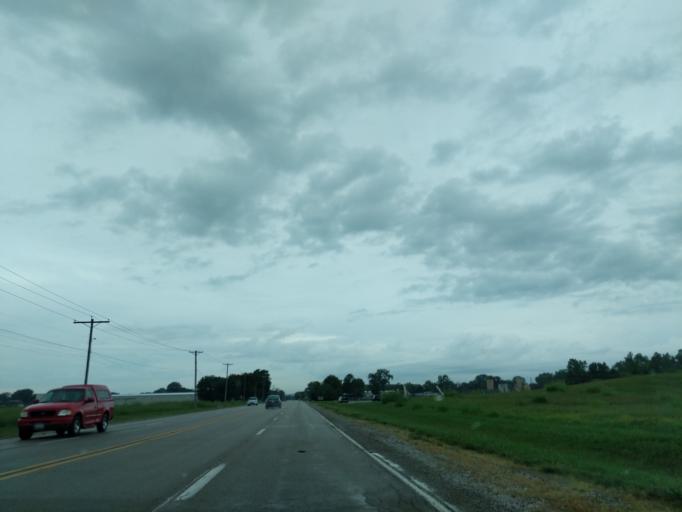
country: US
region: Illinois
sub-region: Saint Clair County
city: Fairmont City
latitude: 38.6591
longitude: -90.0724
